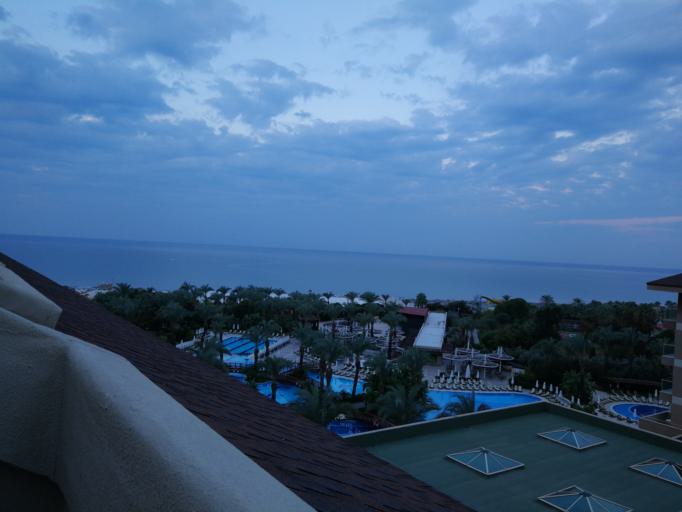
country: TR
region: Antalya
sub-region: Manavgat
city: Side
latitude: 36.8009
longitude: 31.3620
